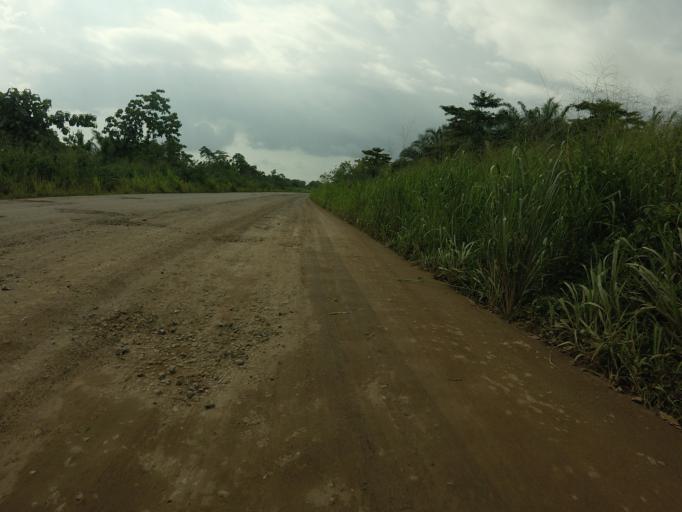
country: GH
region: Volta
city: Kpandu
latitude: 6.9774
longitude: 0.4492
